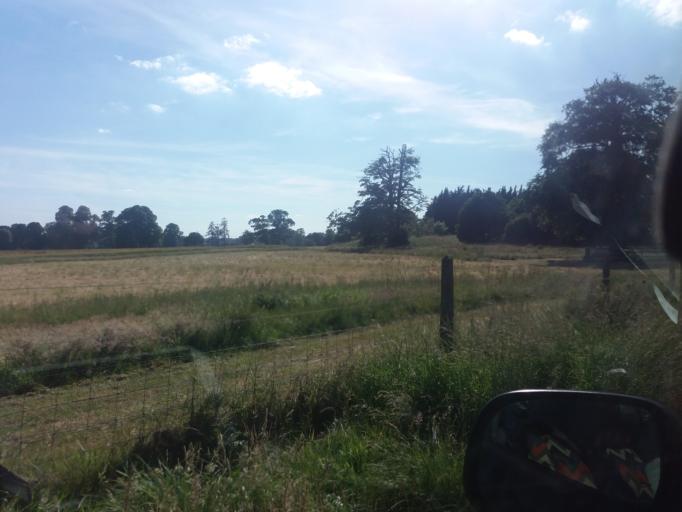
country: IE
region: Leinster
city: Castleknock
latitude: 53.3924
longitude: -6.3538
